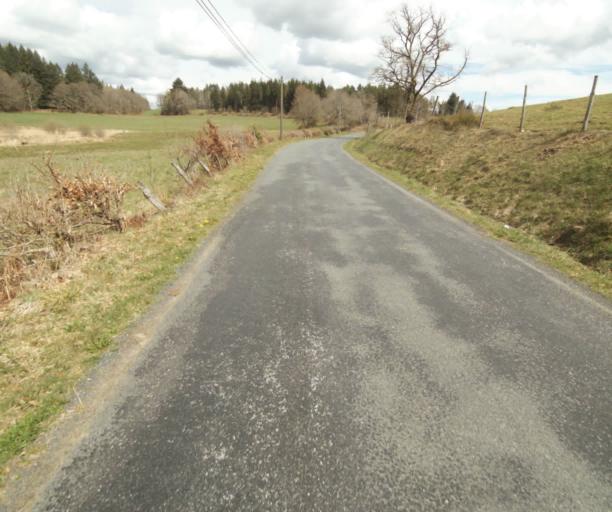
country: FR
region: Limousin
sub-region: Departement de la Correze
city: Correze
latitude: 45.3703
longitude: 1.9316
